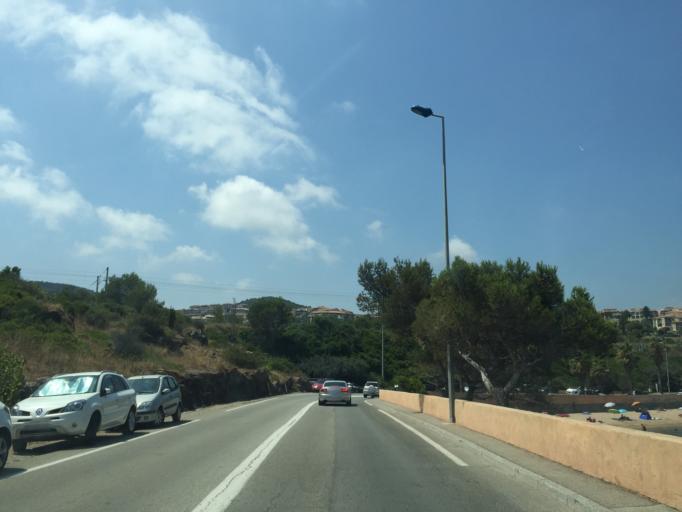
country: FR
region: Provence-Alpes-Cote d'Azur
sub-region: Departement du Var
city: Saint-Raphael
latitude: 43.4242
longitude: 6.8568
